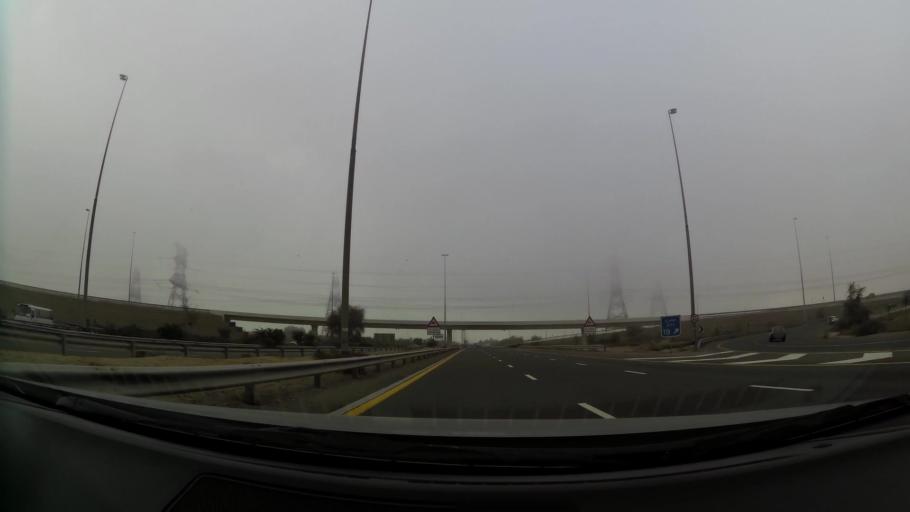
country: AE
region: Dubai
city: Dubai
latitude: 25.0861
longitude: 55.3931
